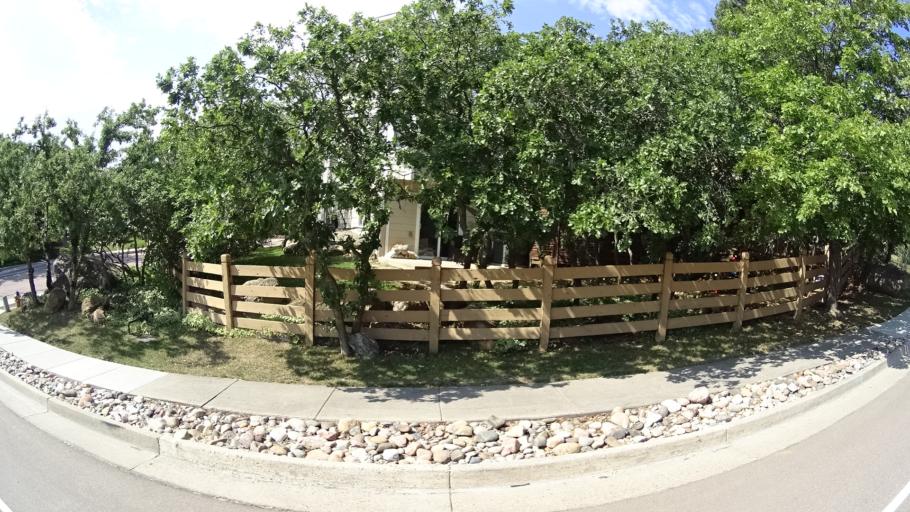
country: US
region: Colorado
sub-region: El Paso County
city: Fort Carson
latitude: 38.7568
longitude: -104.8303
